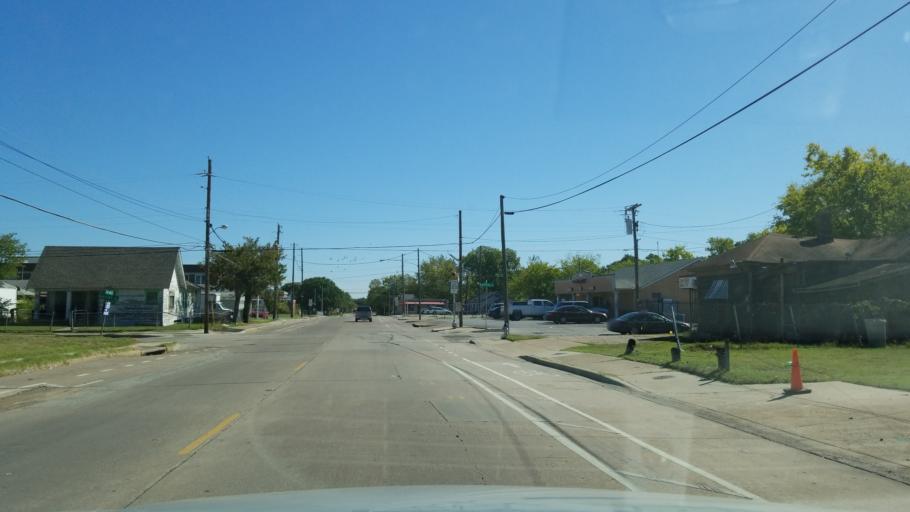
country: US
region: Texas
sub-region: Dallas County
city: Dallas
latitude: 32.7758
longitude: -96.7510
